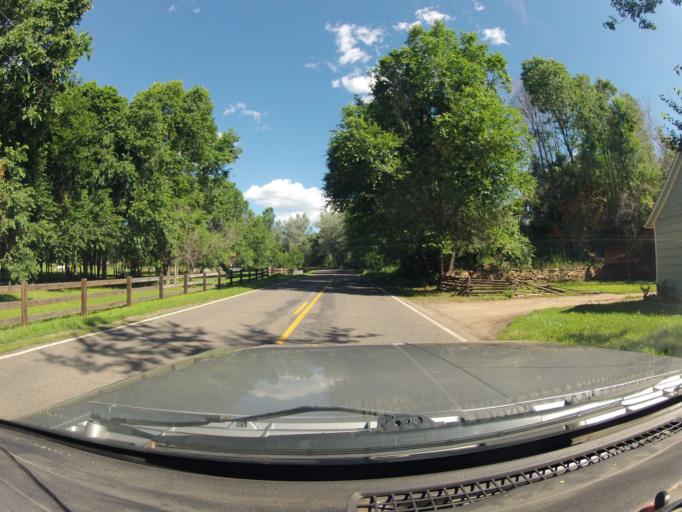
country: US
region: Colorado
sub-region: Larimer County
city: Laporte
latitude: 40.4904
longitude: -105.2174
